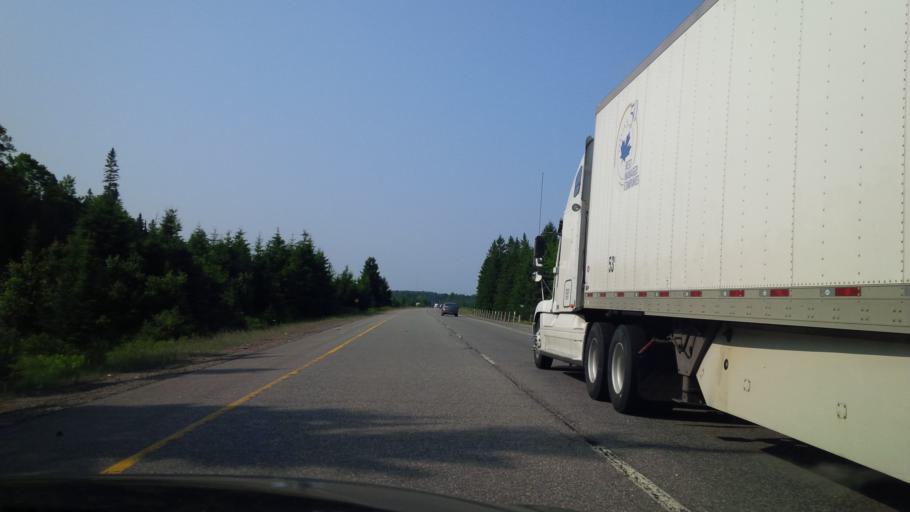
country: CA
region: Ontario
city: Huntsville
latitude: 45.2456
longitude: -79.2988
